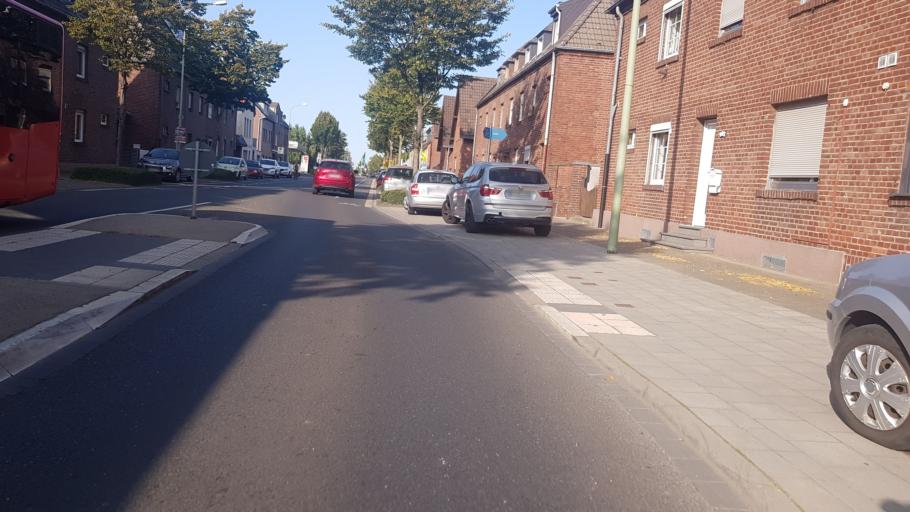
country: DE
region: North Rhine-Westphalia
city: Baesweiler
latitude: 50.9087
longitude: 6.1901
